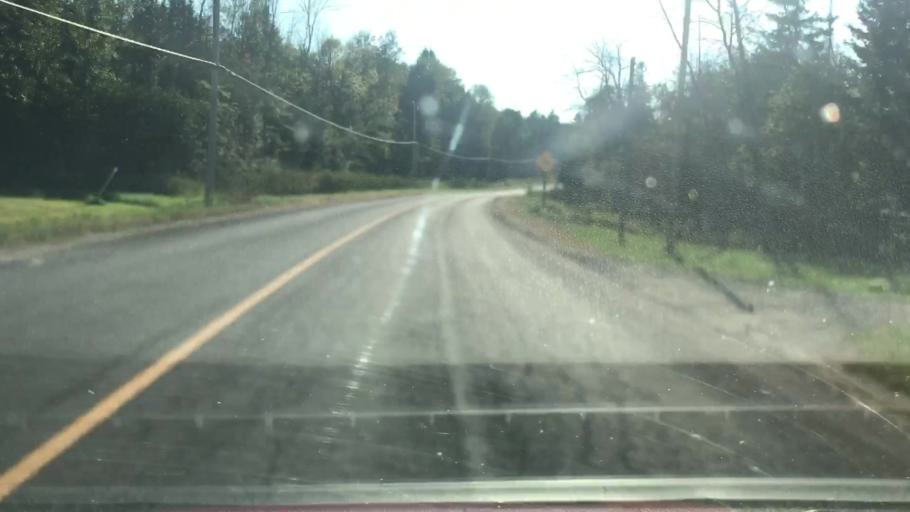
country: US
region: Michigan
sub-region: Chippewa County
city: Sault Ste. Marie
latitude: 46.2901
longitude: -84.0414
